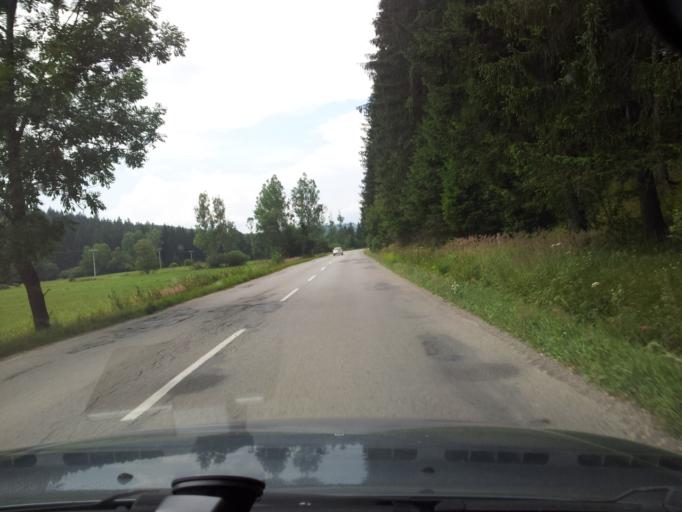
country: SK
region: Zilinsky
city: Oravska Lesna
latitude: 49.3765
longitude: 19.2594
